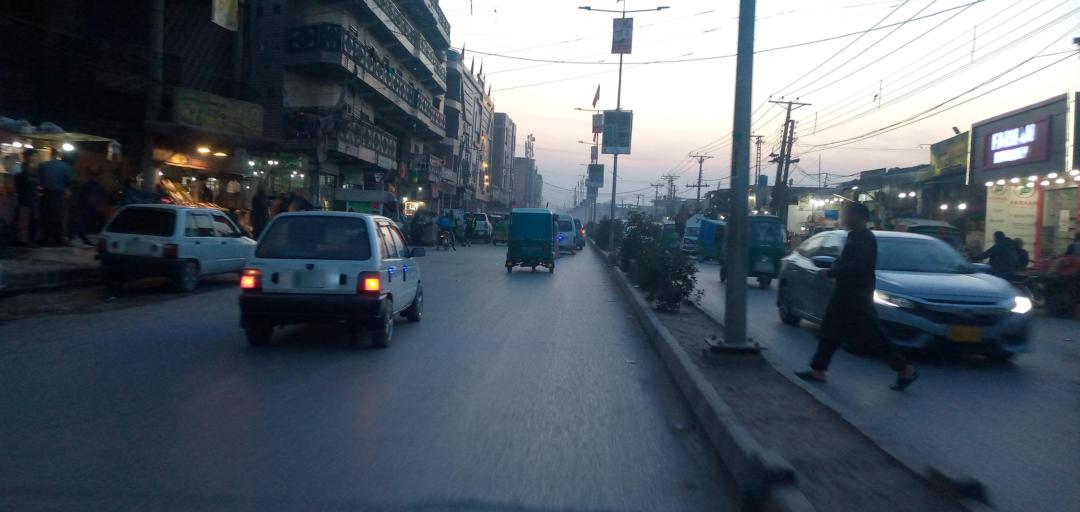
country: PK
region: Khyber Pakhtunkhwa
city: Peshawar
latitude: 34.0291
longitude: 71.6015
